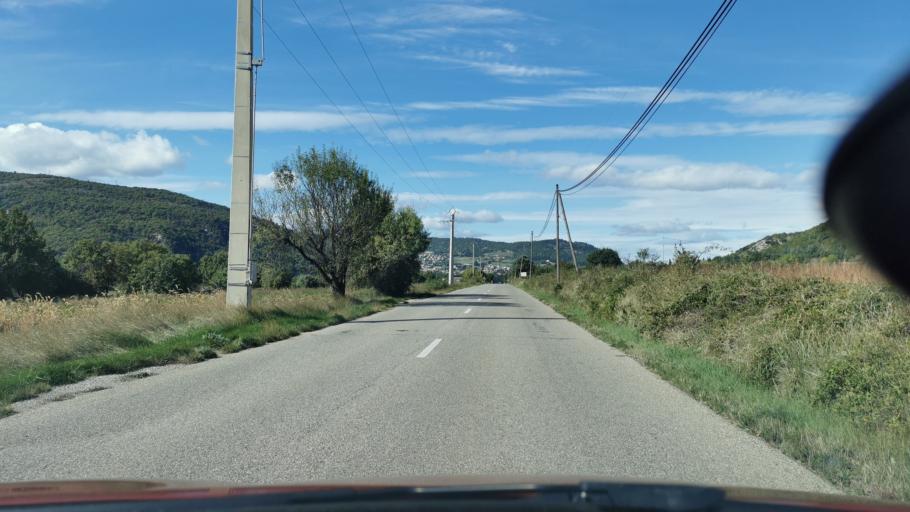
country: FR
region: Provence-Alpes-Cote d'Azur
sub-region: Departement des Alpes-de-Haute-Provence
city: Peipin
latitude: 44.1639
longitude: 5.9625
